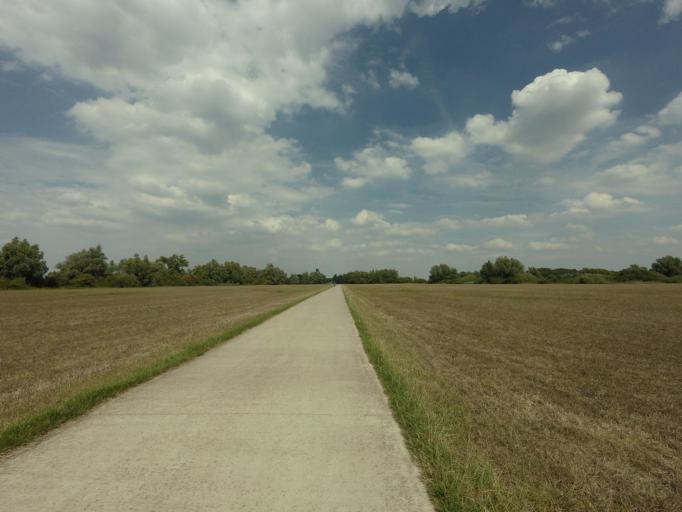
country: NL
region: Gelderland
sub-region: Gemeente Doesburg
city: Doesburg
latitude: 52.0177
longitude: 6.1174
